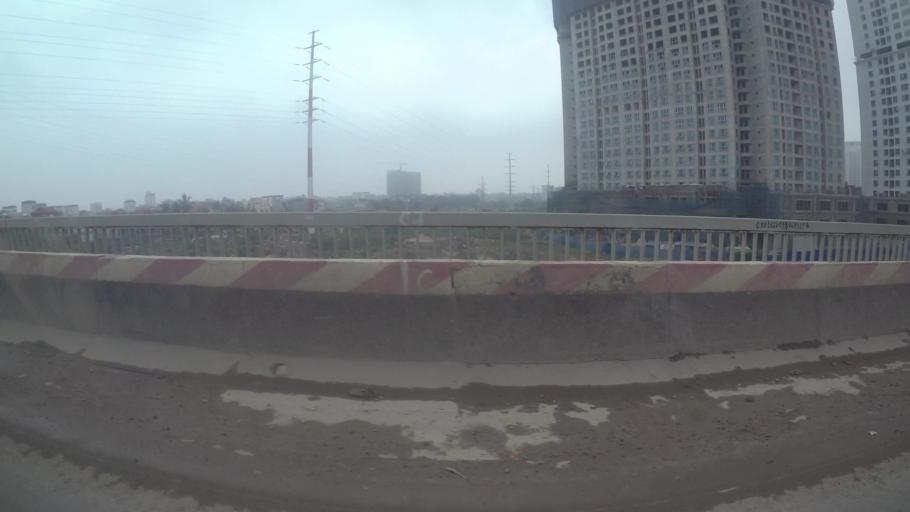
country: VN
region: Ha Noi
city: Tay Ho
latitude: 21.0863
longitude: 105.7871
